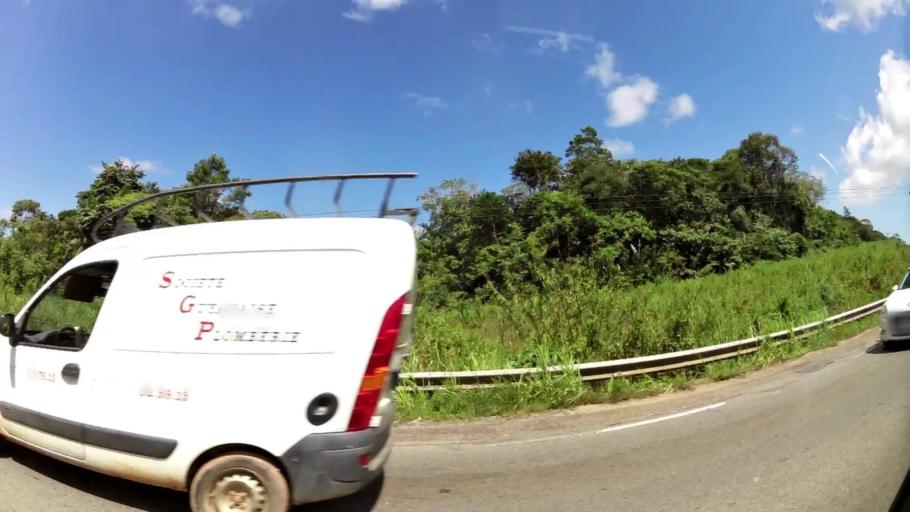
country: GF
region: Guyane
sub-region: Guyane
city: Matoury
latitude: 4.8649
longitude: -52.3335
